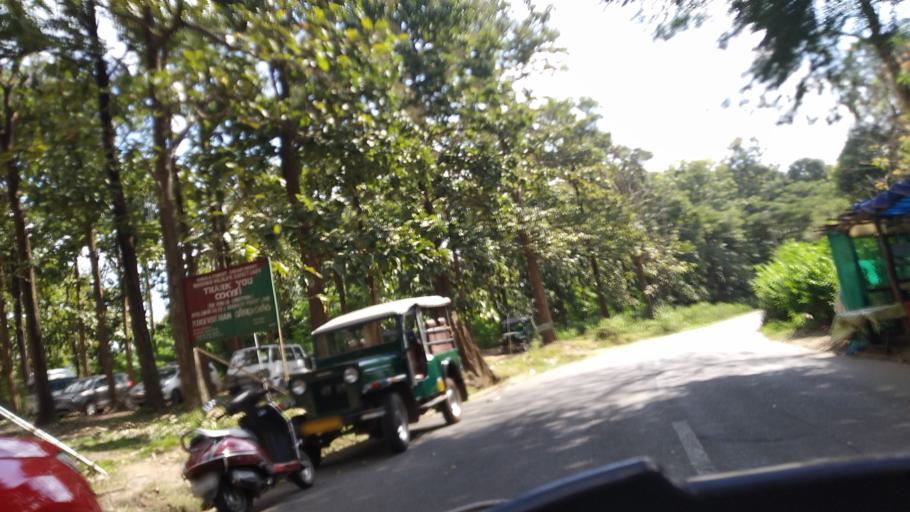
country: IN
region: Kerala
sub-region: Wayanad
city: Panamaram
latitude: 11.9434
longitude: 76.0648
